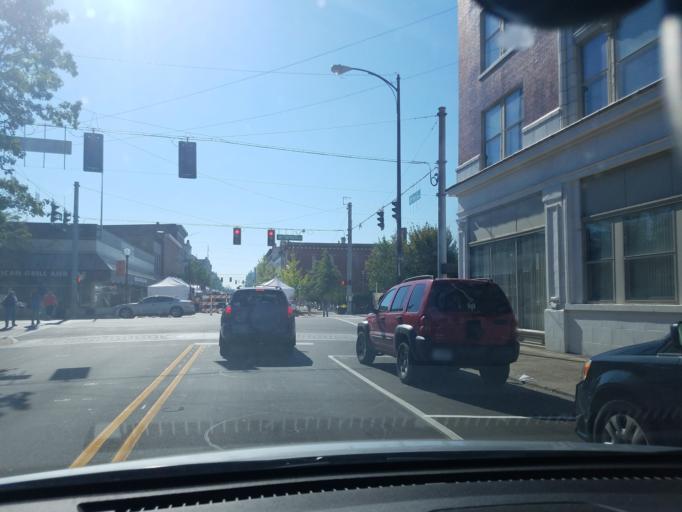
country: US
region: Indiana
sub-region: Floyd County
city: New Albany
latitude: 38.2863
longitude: -85.8232
